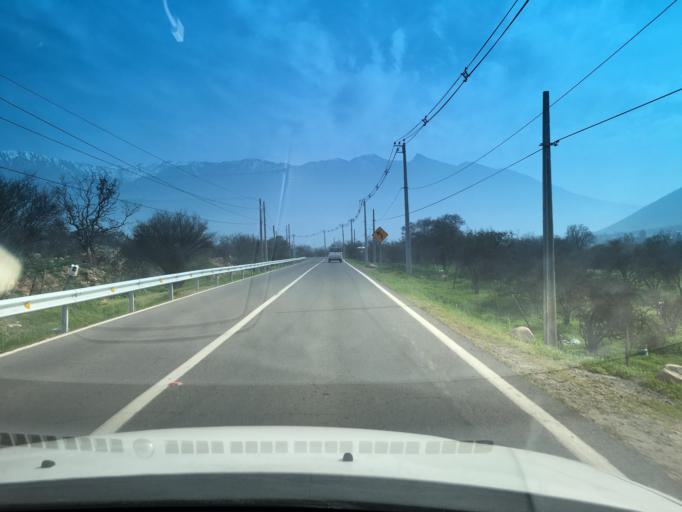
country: CL
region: Santiago Metropolitan
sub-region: Provincia de Chacabuco
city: Lampa
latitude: -33.2519
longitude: -70.9075
